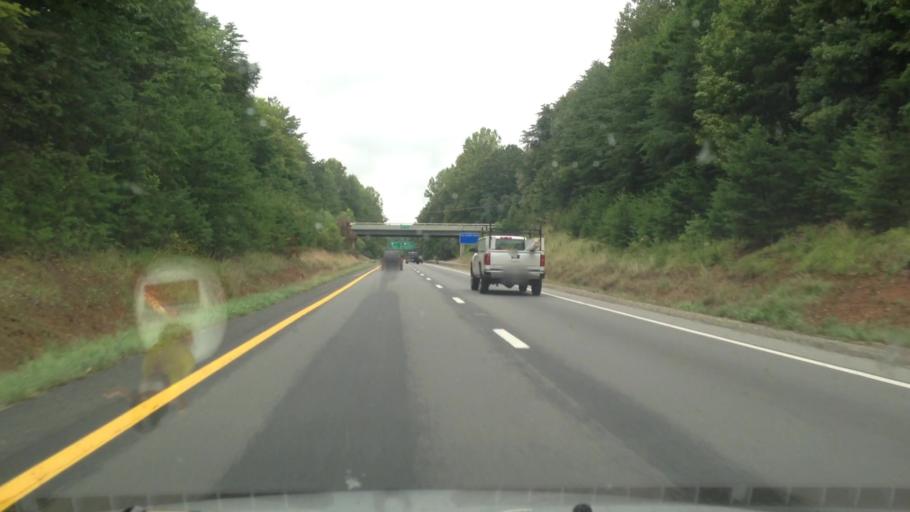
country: US
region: Virginia
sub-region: Henry County
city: Horse Pasture
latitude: 36.6420
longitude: -79.8980
